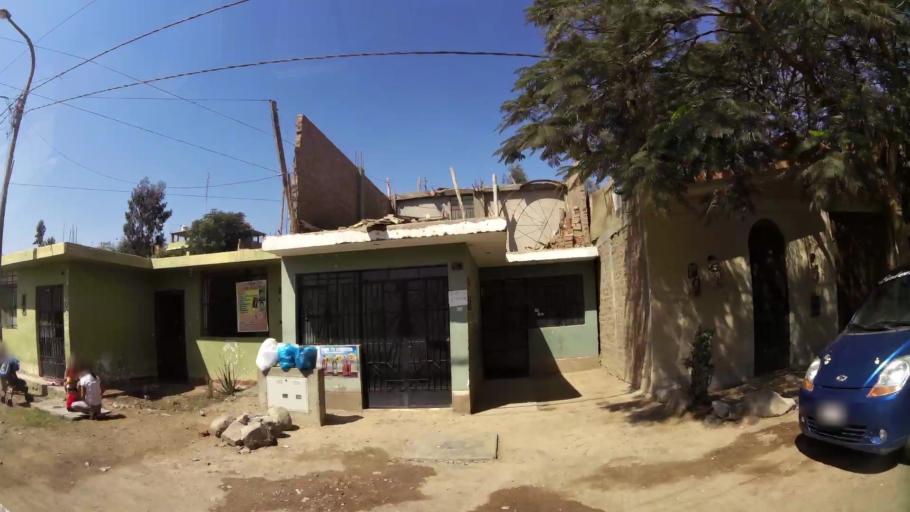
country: PE
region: Ica
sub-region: Provincia de Ica
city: Subtanjalla
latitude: -14.0418
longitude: -75.7496
